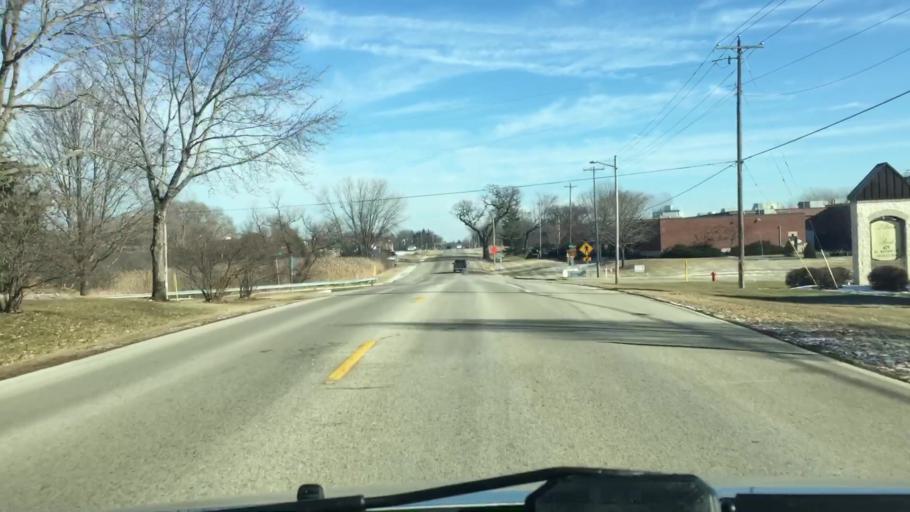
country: US
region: Wisconsin
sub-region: Waukesha County
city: Mukwonago
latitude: 42.8688
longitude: -88.3227
